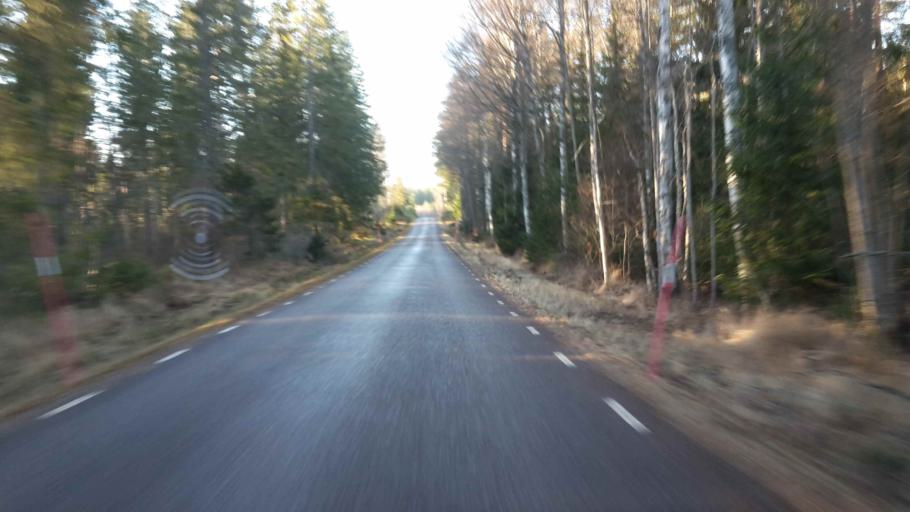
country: SE
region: Kalmar
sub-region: Vasterviks Kommun
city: Overum
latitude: 58.1527
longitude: 16.2766
